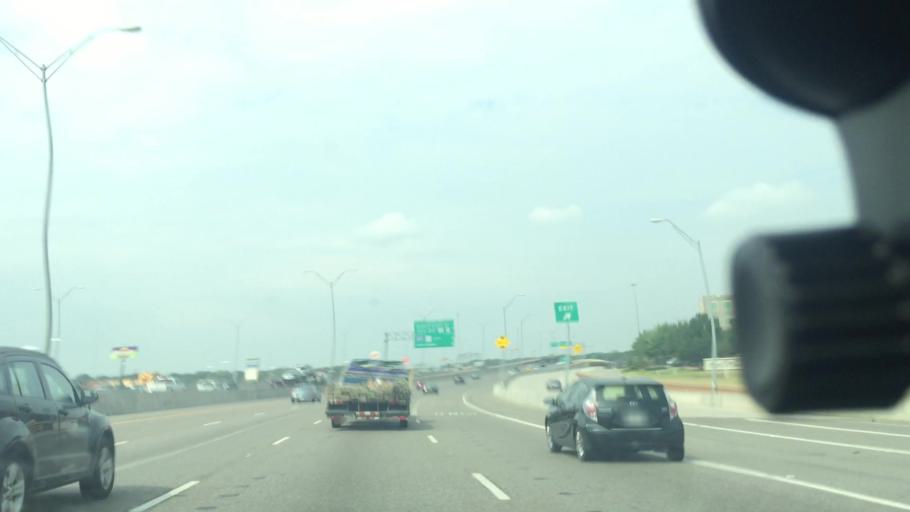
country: US
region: Texas
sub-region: Tarrant County
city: Bedford
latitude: 32.8372
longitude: -97.1448
